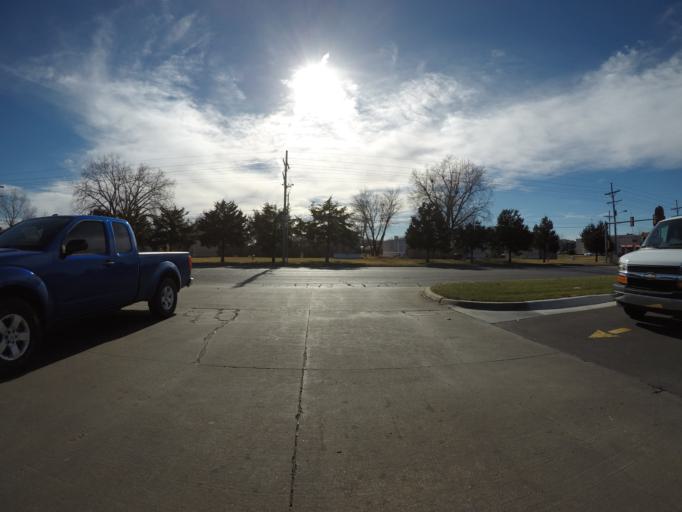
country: US
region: Kansas
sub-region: Reno County
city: Hutchinson
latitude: 38.0651
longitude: -97.8985
